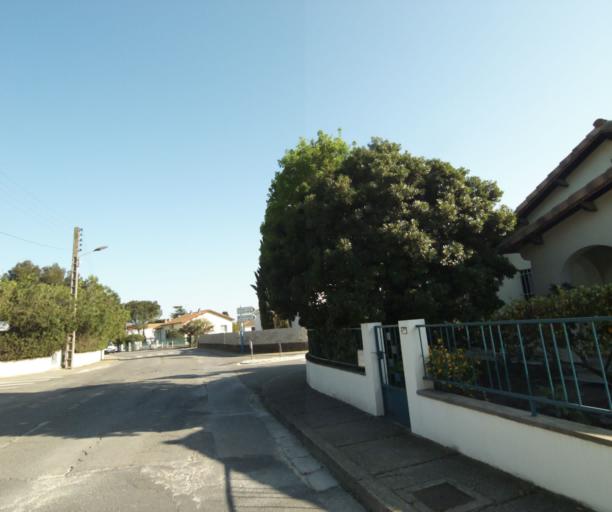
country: FR
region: Languedoc-Roussillon
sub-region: Departement de l'Herault
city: Castelnau-le-Lez
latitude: 43.6367
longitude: 3.9105
